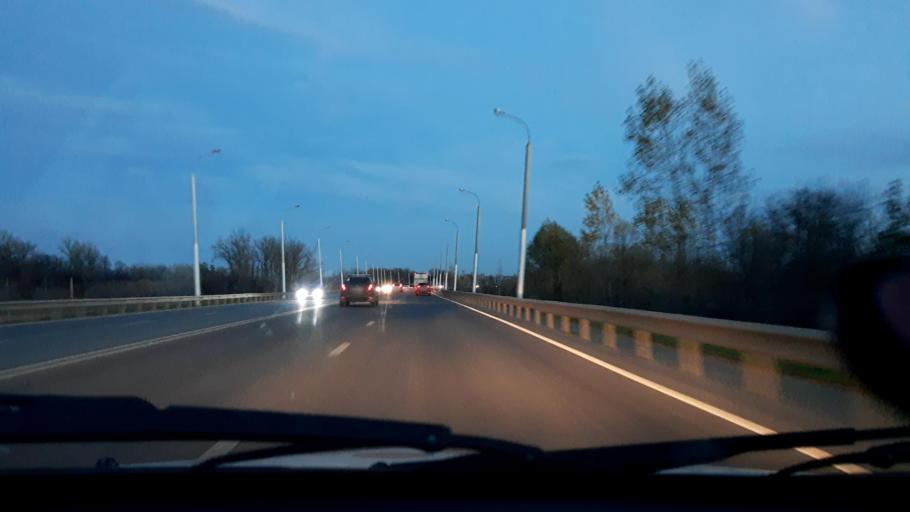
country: RU
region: Bashkortostan
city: Iglino
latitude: 54.8008
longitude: 56.1964
